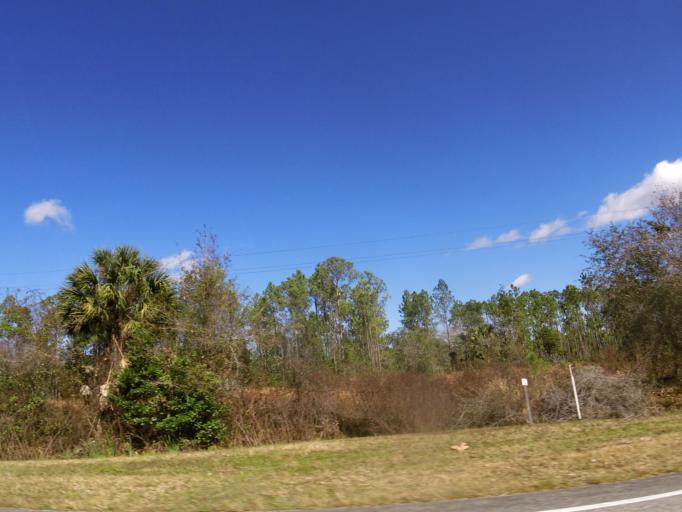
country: US
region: Florida
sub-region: Volusia County
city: De Leon Springs
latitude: 29.1753
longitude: -81.4057
